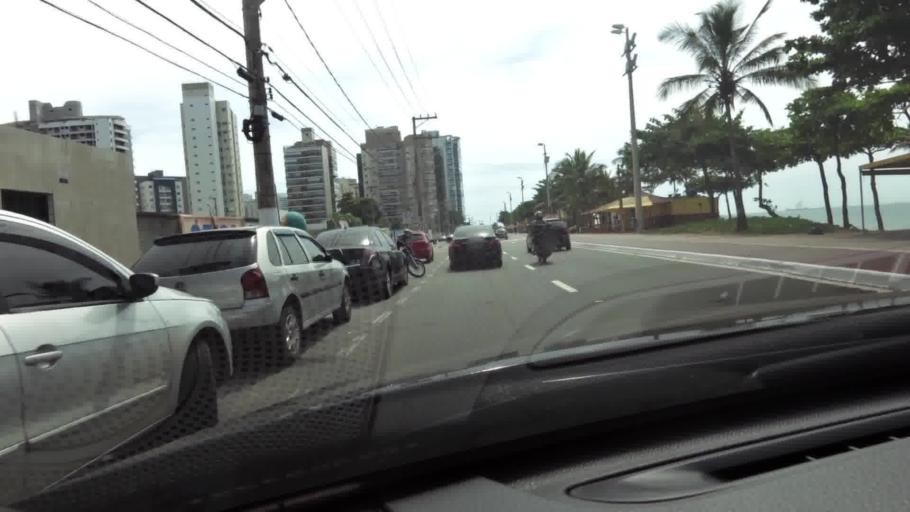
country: BR
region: Espirito Santo
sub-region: Vila Velha
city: Vila Velha
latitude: -20.3576
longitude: -40.2912
